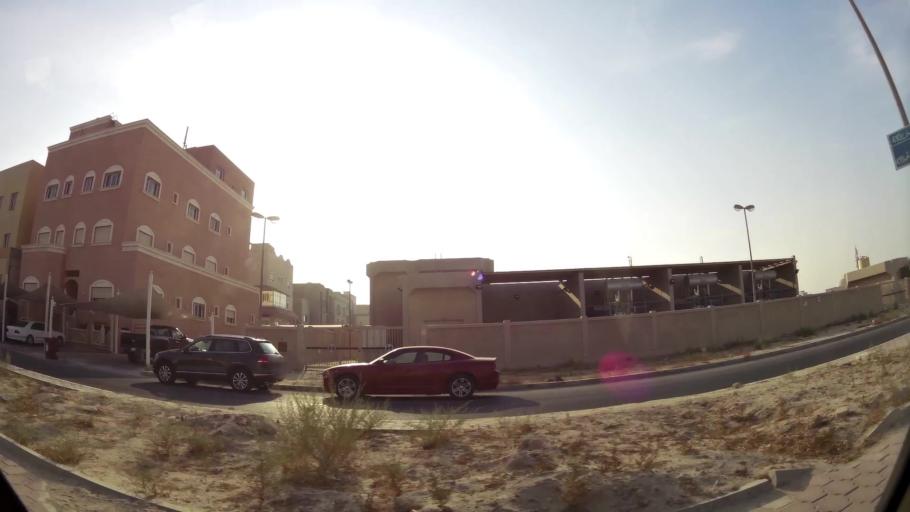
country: KW
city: Al Funaytis
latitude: 29.2355
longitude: 48.0880
